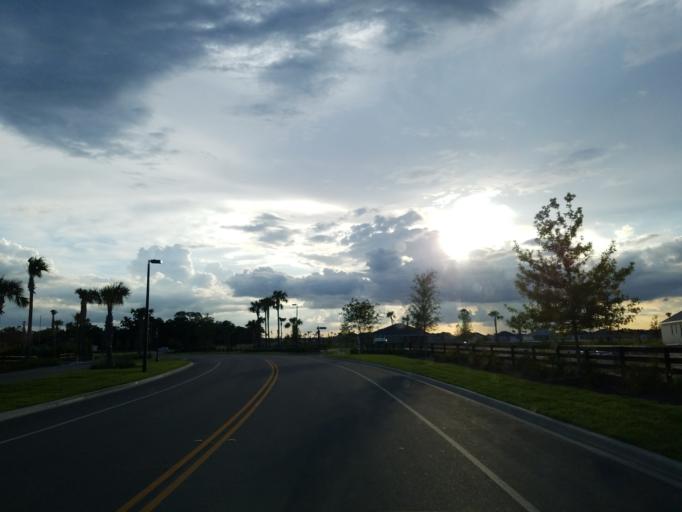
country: US
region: Florida
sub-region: Sumter County
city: Wildwood
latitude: 28.7906
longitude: -82.0157
